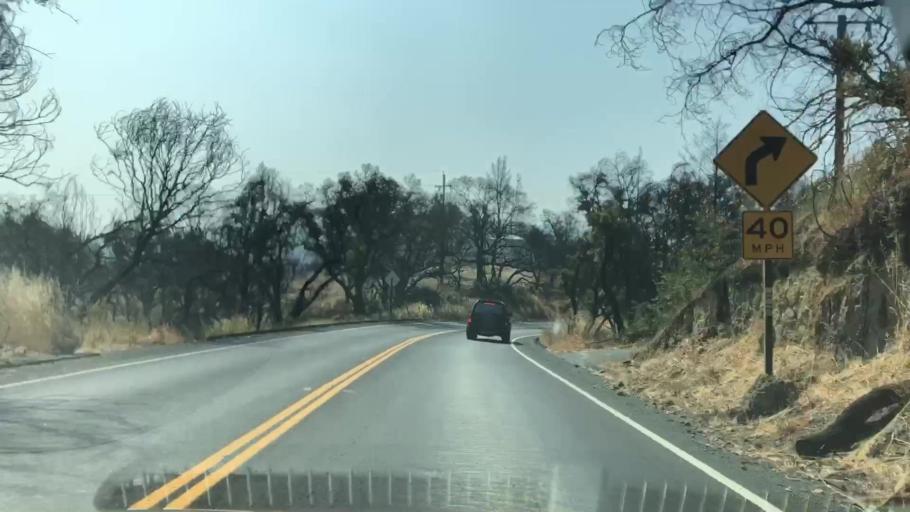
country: US
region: California
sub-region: Sonoma County
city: Larkfield-Wikiup
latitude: 38.5151
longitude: -122.7191
